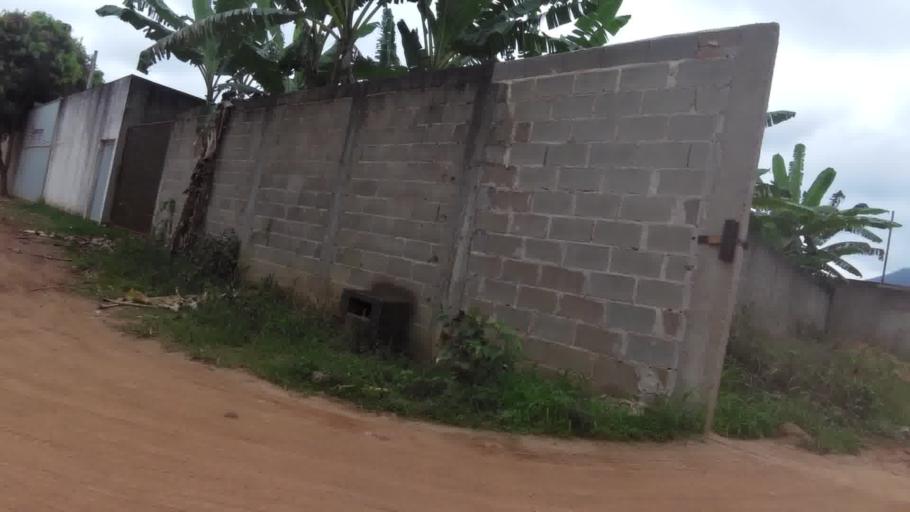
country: BR
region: Espirito Santo
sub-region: Alfredo Chaves
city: Alfredo Chaves
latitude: -20.6391
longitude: -40.7434
